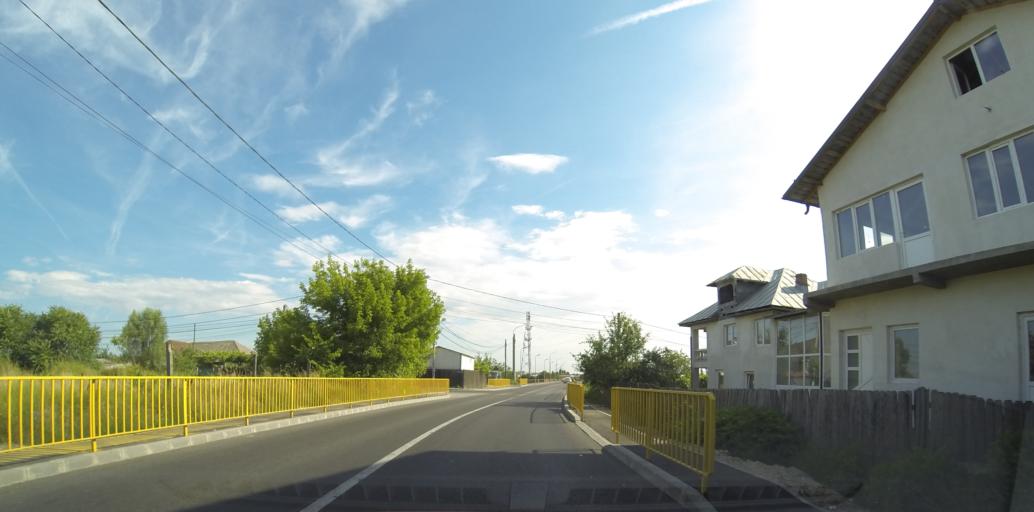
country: RO
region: Dolj
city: Craiova
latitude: 44.3397
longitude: 23.7948
